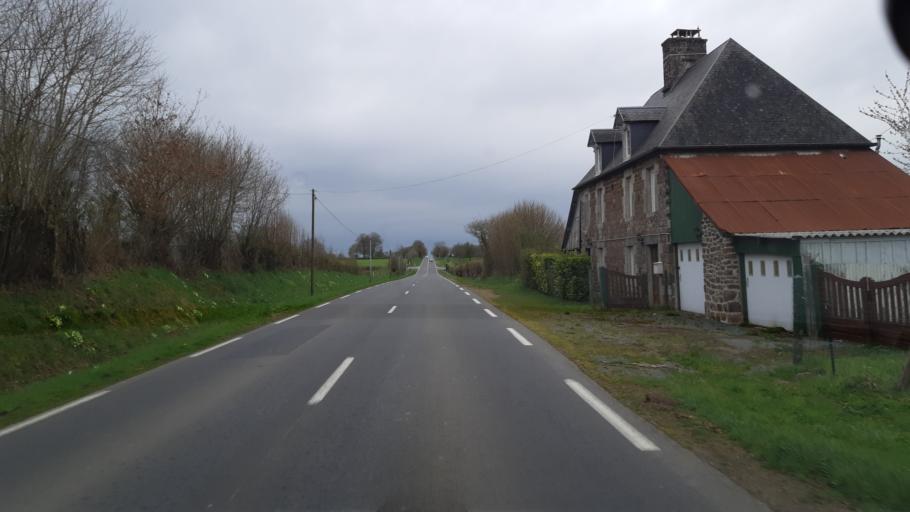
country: FR
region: Lower Normandy
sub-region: Departement de la Manche
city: Hambye
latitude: 48.9522
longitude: -1.2339
